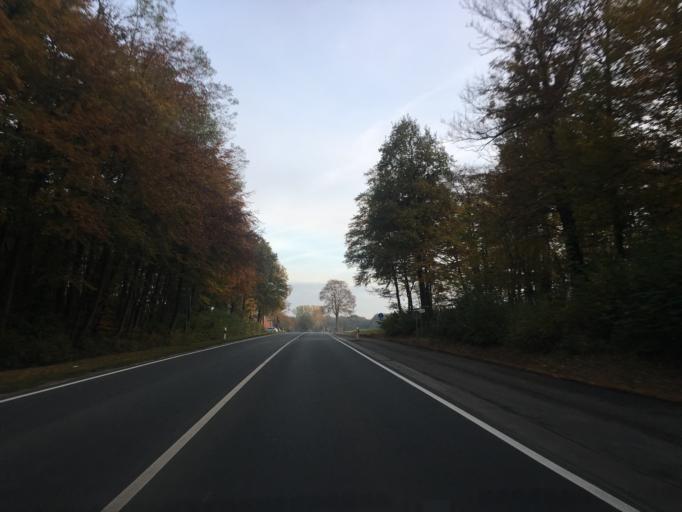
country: DE
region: North Rhine-Westphalia
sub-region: Regierungsbezirk Munster
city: Steinfurt
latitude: 52.1364
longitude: 7.3706
